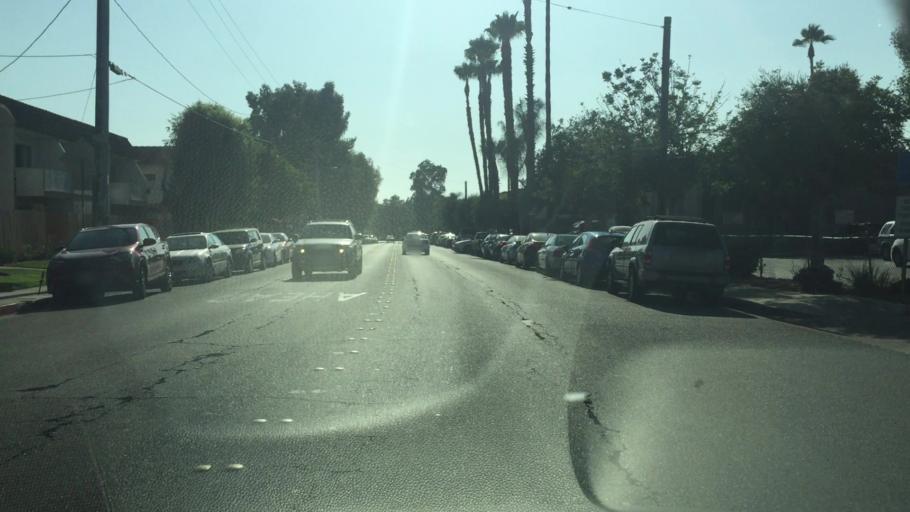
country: US
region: California
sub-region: San Diego County
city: El Cajon
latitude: 32.7929
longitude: -116.9455
